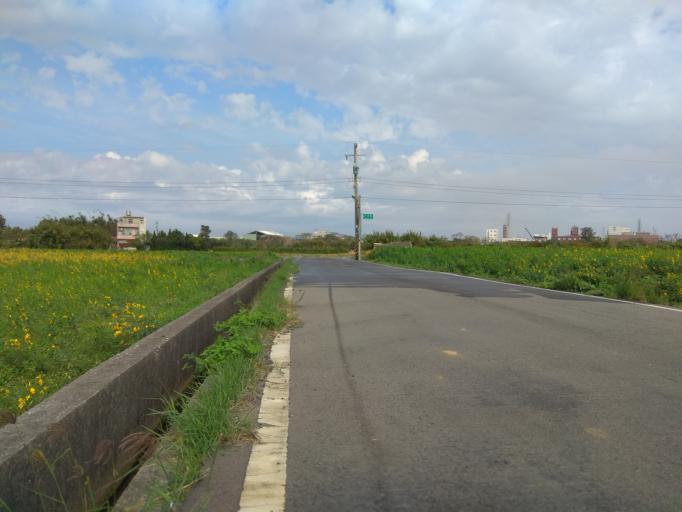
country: TW
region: Taiwan
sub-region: Hsinchu
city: Zhubei
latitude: 24.9798
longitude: 121.0323
